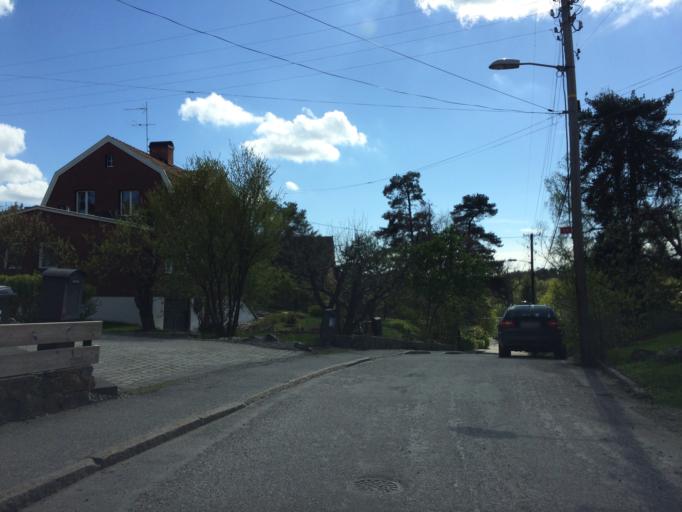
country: SE
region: Stockholm
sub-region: Huddinge Kommun
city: Segeltorp
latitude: 59.3025
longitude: 17.9626
